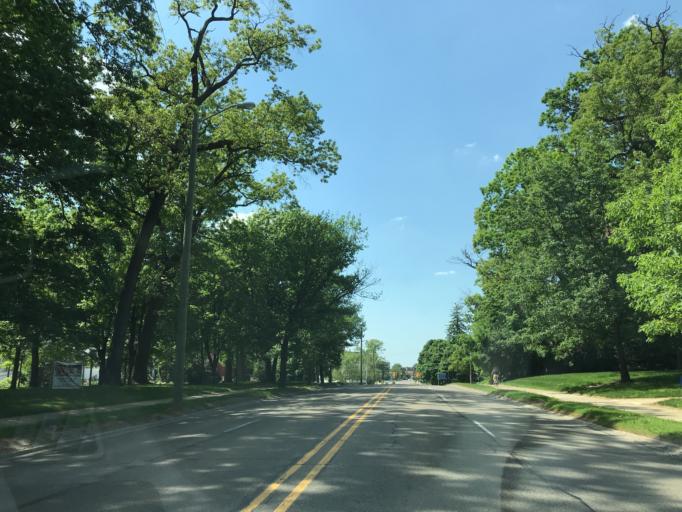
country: US
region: Michigan
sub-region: Washtenaw County
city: Ann Arbor
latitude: 42.2738
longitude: -83.7297
